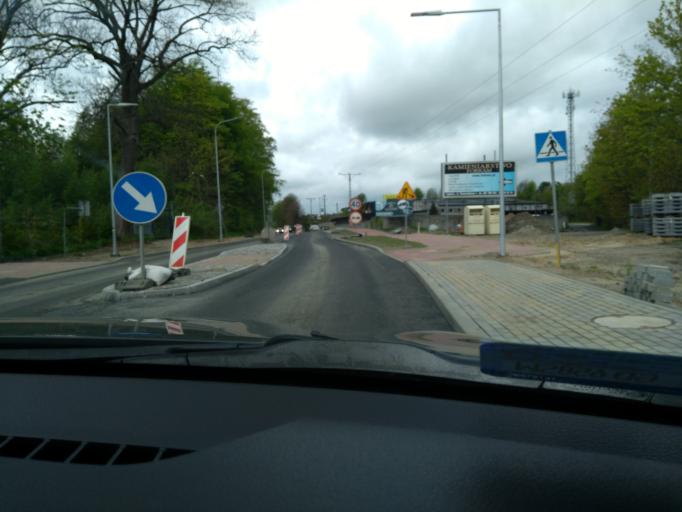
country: PL
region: Pomeranian Voivodeship
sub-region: Powiat kartuski
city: Kartuzy
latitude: 54.3443
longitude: 18.1580
